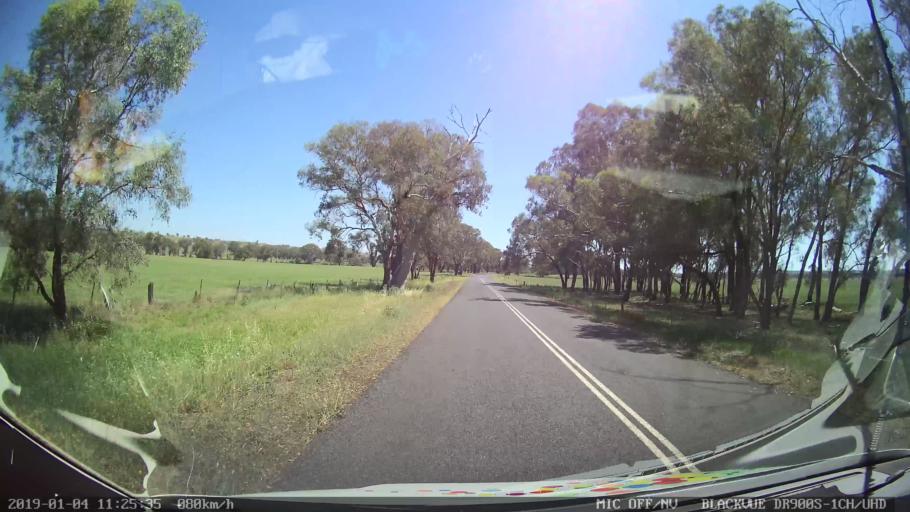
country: AU
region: New South Wales
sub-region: Cabonne
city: Molong
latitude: -33.1231
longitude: 148.7523
